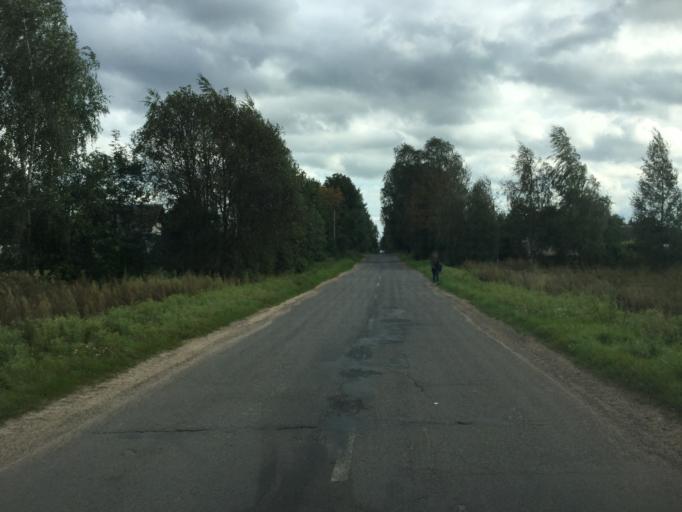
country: BY
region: Vitebsk
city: Vitebsk
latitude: 55.1472
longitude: 30.2810
